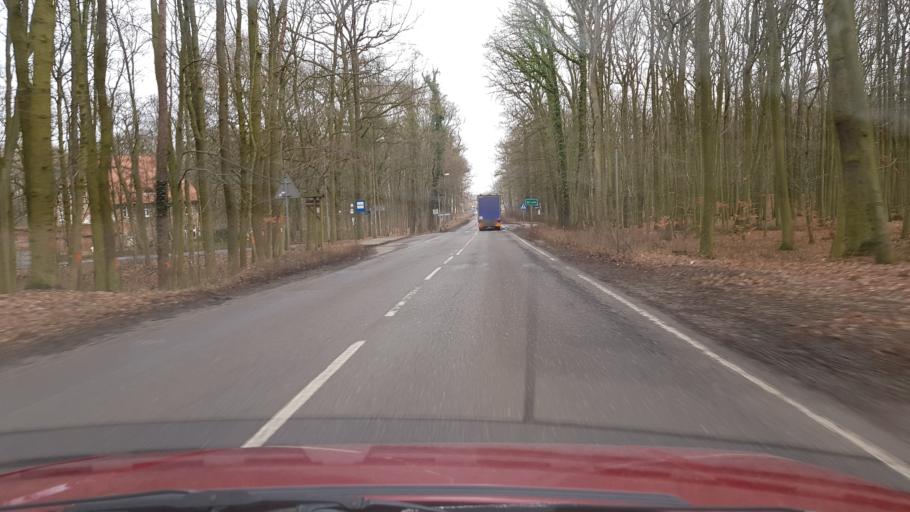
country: PL
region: West Pomeranian Voivodeship
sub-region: Powiat policki
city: Police
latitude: 53.5327
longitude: 14.5757
